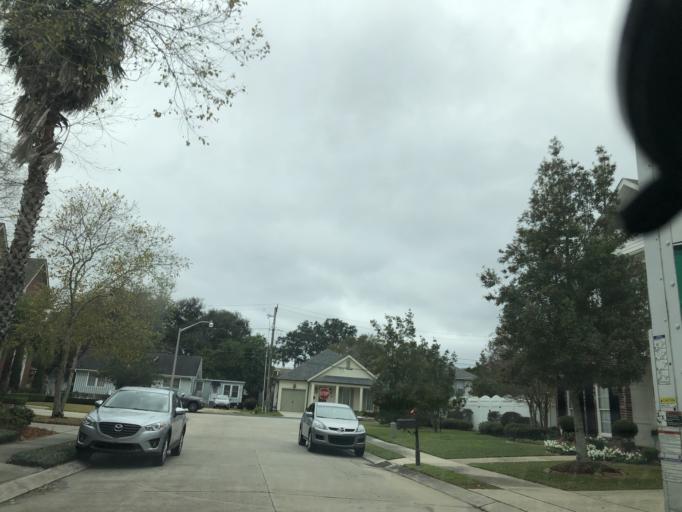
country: US
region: Louisiana
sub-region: Jefferson Parish
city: Metairie
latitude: 29.9778
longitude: -90.1513
